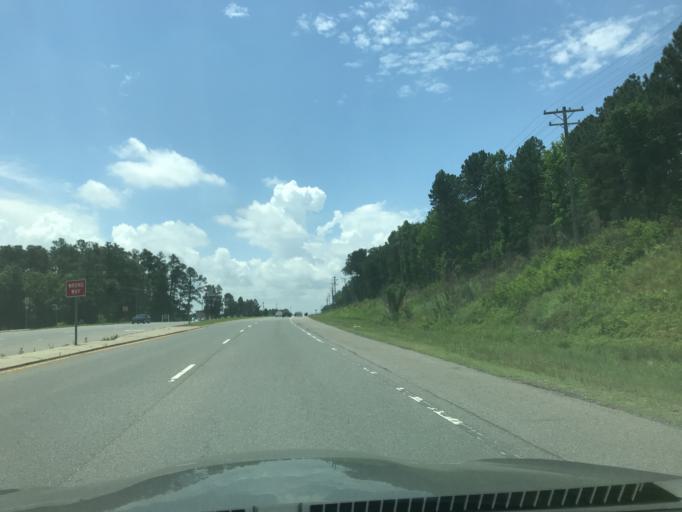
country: US
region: North Carolina
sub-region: Wake County
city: Morrisville
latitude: 35.8730
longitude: -78.8915
